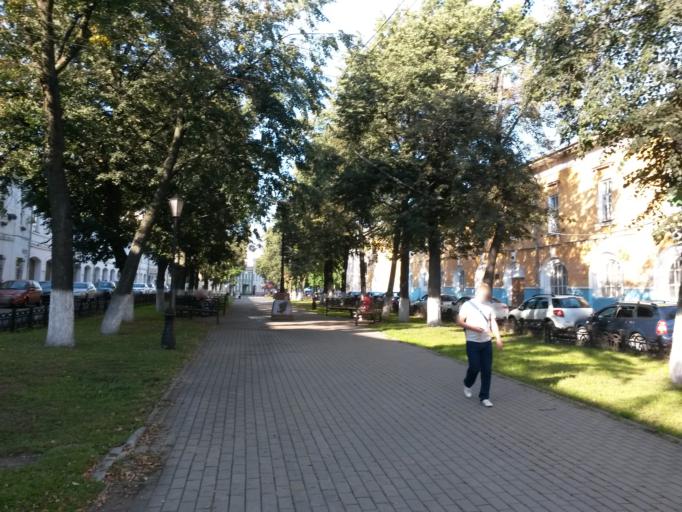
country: RU
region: Jaroslavl
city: Yaroslavl
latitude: 57.6227
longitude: 39.8919
